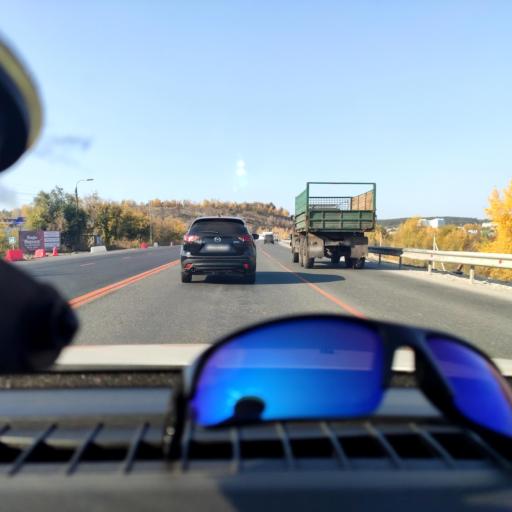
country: RU
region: Samara
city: Volzhskiy
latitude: 53.4167
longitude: 50.1298
